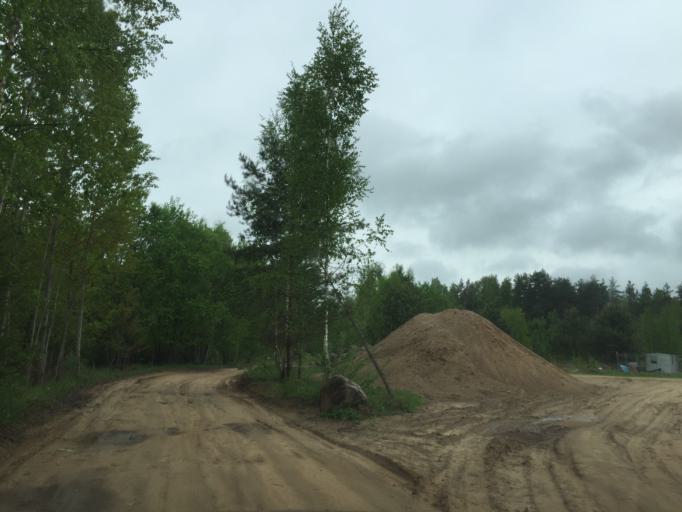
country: LV
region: Kegums
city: Kegums
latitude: 56.7380
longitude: 24.7621
